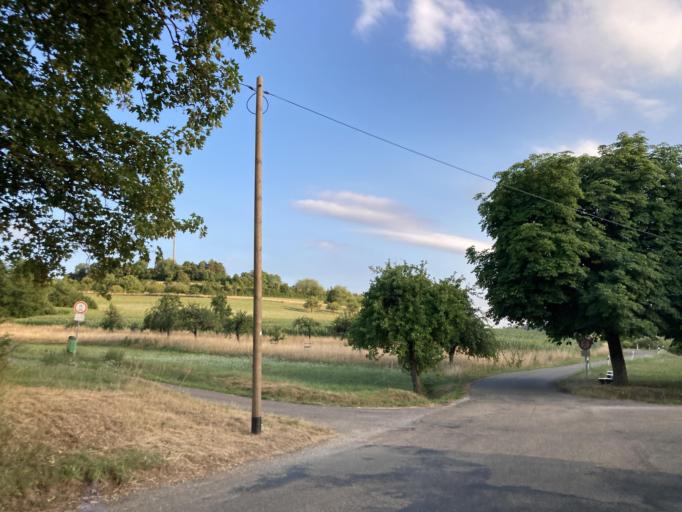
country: DE
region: Baden-Wuerttemberg
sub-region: Karlsruhe Region
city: Ebhausen
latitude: 48.5943
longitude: 8.6816
